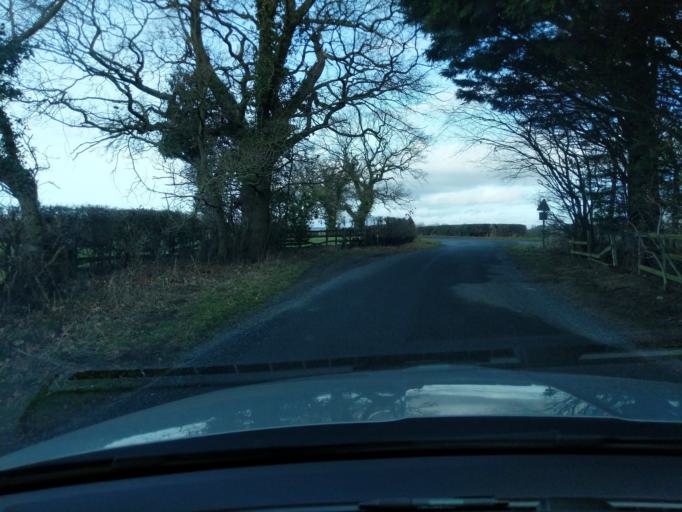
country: GB
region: England
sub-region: North Yorkshire
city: Catterick
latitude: 54.3786
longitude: -1.6717
